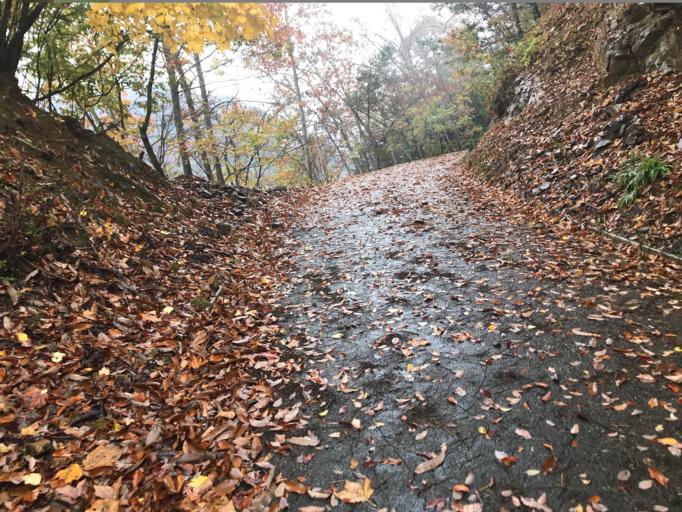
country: JP
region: Kyoto
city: Maizuru
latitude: 35.3232
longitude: 135.4606
